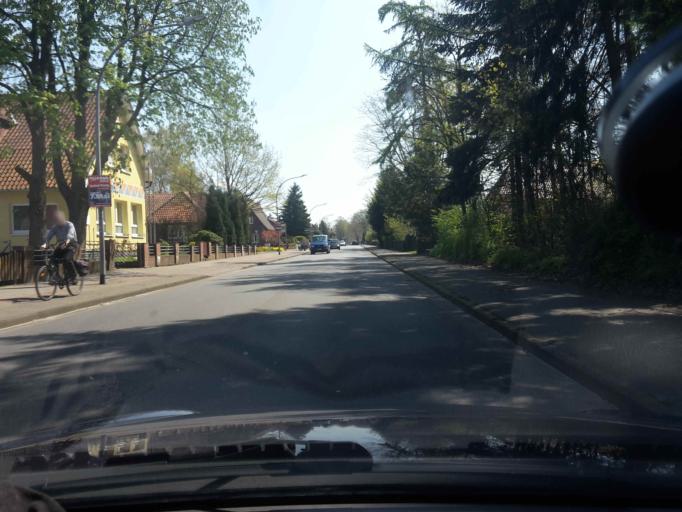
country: DE
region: Lower Saxony
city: Schneverdingen
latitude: 53.1119
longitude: 9.8003
